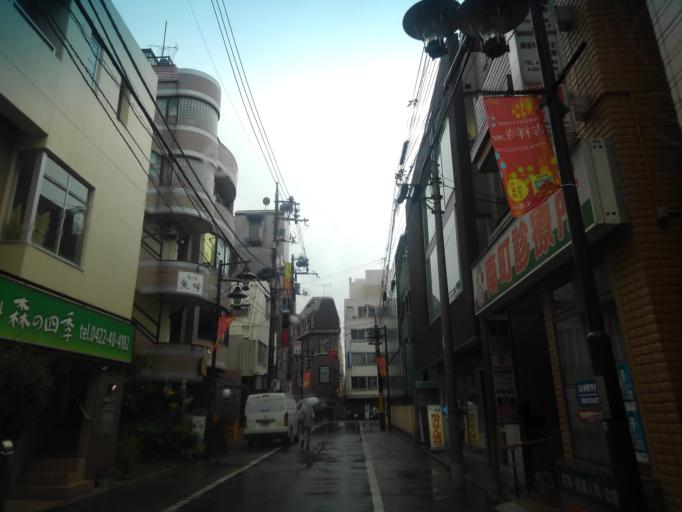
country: JP
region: Tokyo
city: Musashino
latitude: 35.7022
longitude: 139.5821
